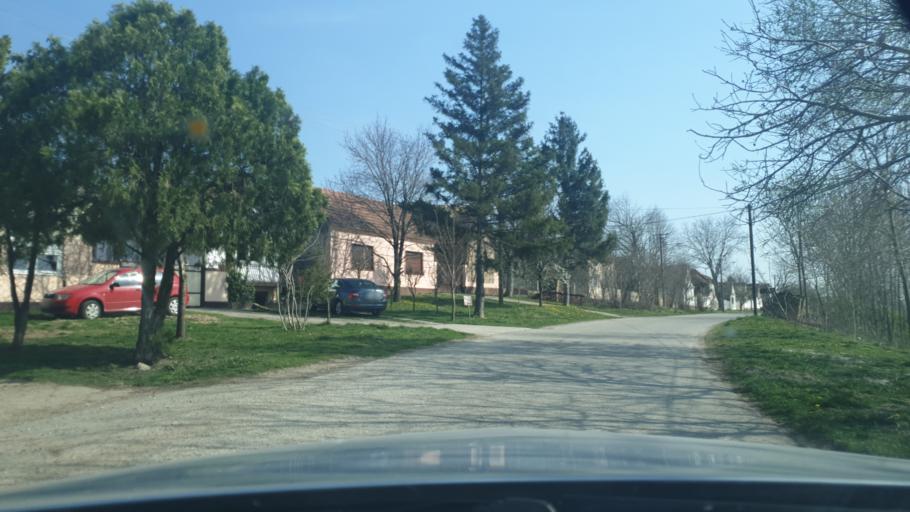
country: RS
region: Autonomna Pokrajina Vojvodina
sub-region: Sremski Okrug
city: Irig
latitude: 45.0660
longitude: 19.9228
